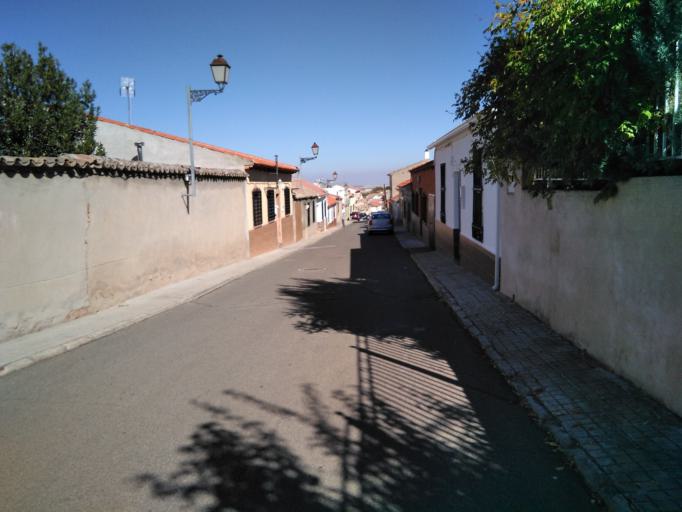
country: ES
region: Castille-La Mancha
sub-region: Provincia de Ciudad Real
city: Ballesteros de Calatrava
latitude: 38.8321
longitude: -3.9465
